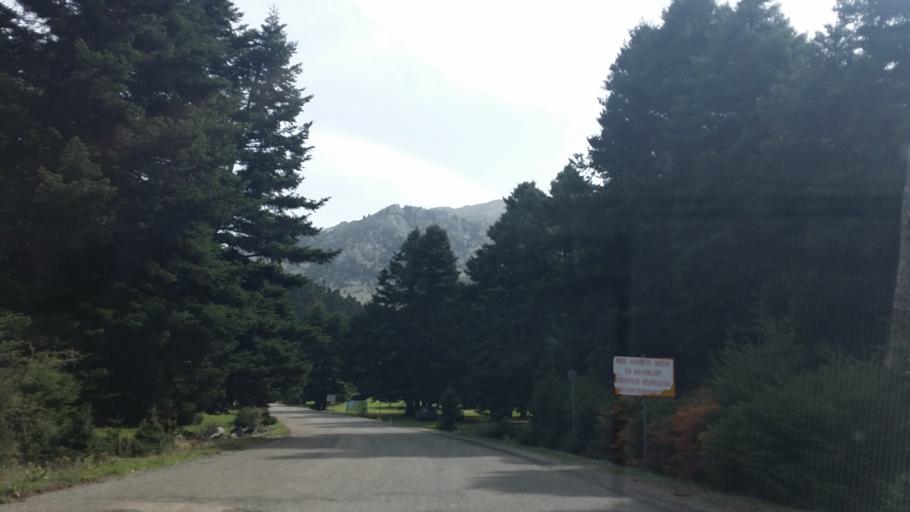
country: GR
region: Central Greece
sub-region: Nomos Voiotias
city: Ayia Trias
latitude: 38.3234
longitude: 22.8525
